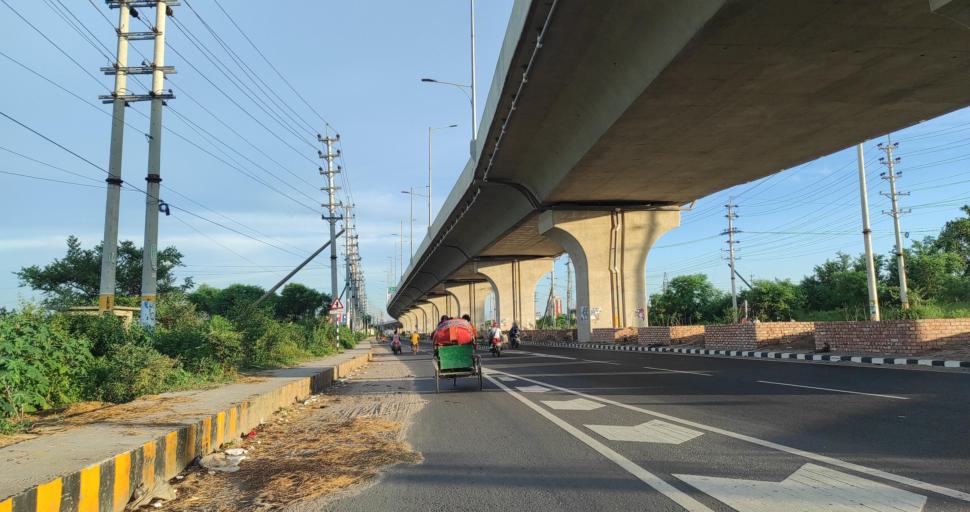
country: BD
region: Dhaka
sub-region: Dhaka
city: Dhaka
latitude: 23.6825
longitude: 90.4030
